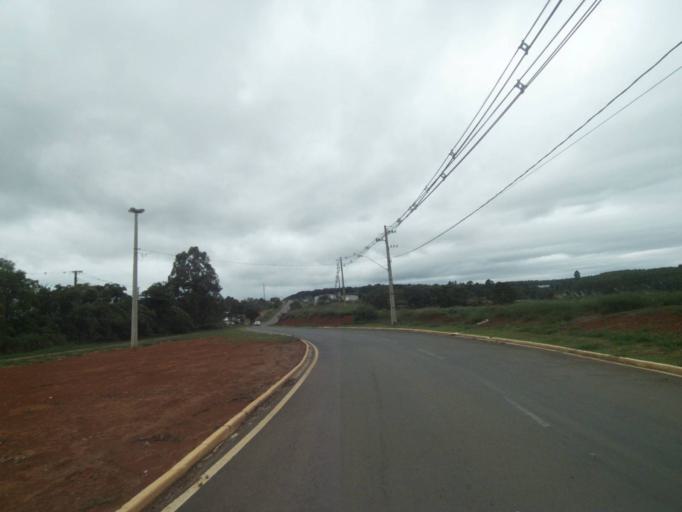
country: BR
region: Parana
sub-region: Telemaco Borba
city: Telemaco Borba
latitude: -24.3846
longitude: -50.6750
